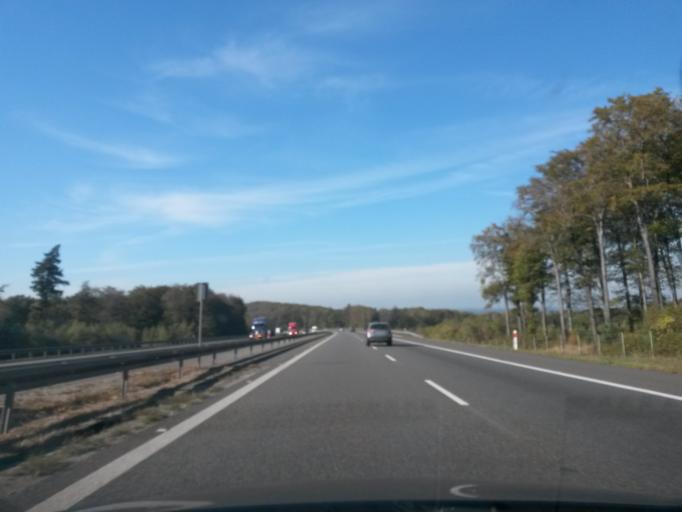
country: PL
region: Opole Voivodeship
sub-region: Powiat krapkowicki
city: Zdzieszowice
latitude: 50.4745
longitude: 18.1381
